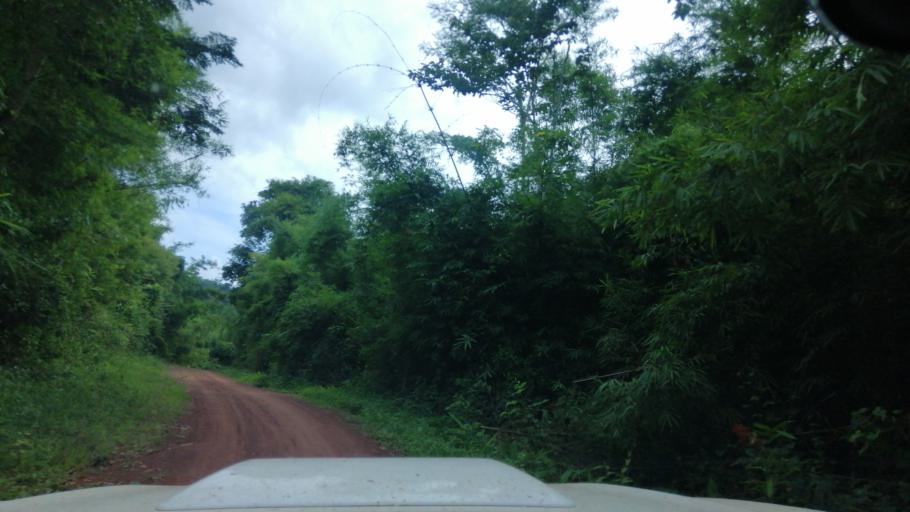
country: TH
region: Nan
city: Mae Charim
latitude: 18.7709
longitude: 101.3127
